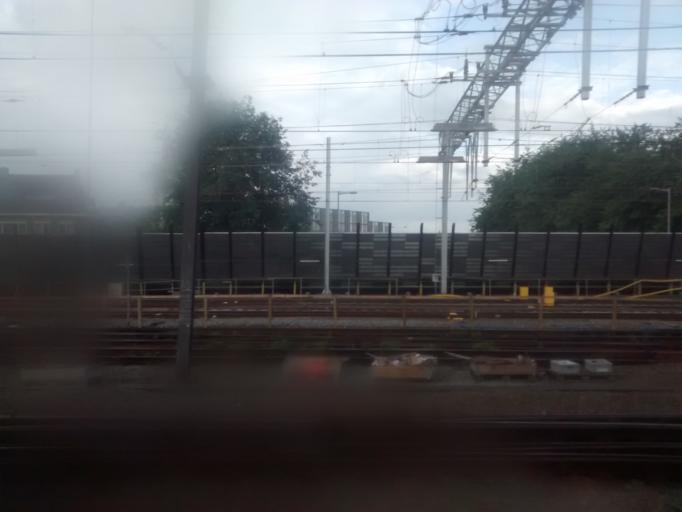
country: NL
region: Utrecht
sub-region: Gemeente Utrecht
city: Utrecht
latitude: 52.0935
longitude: 5.1066
